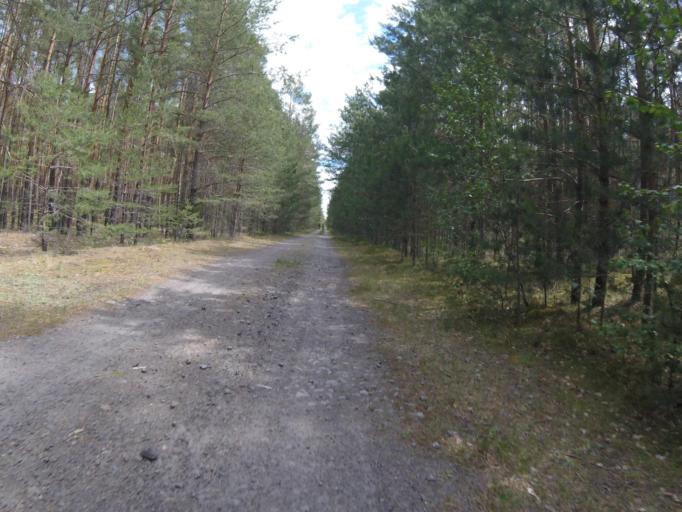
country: DE
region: Brandenburg
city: Halbe
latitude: 52.1027
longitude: 13.6797
